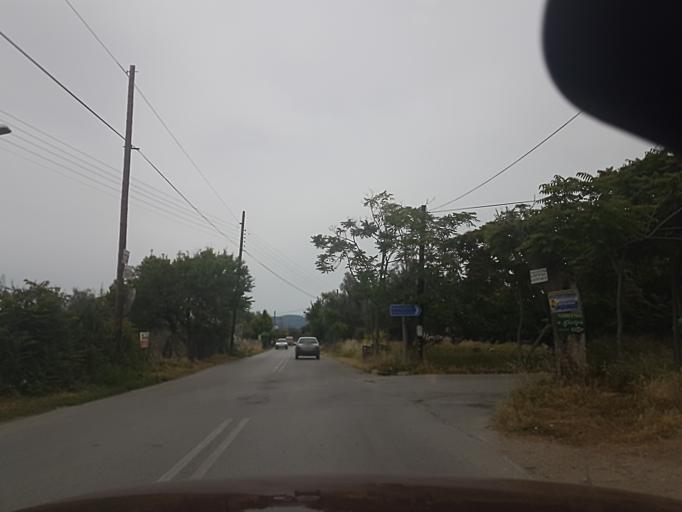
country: GR
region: Central Greece
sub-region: Nomos Evvoias
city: Chalkida
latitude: 38.4650
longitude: 23.6303
